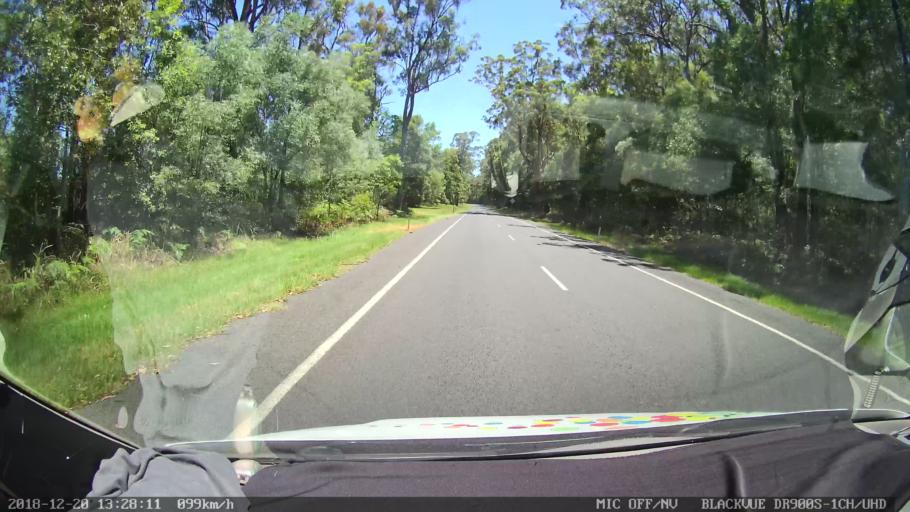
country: AU
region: New South Wales
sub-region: Clarence Valley
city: Gordon
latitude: -29.1711
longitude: 152.9915
